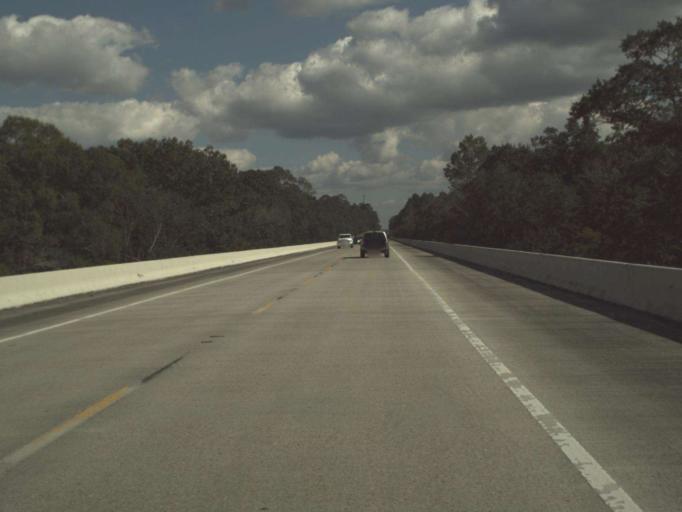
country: US
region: Florida
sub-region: Bay County
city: Laguna Beach
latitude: 30.4503
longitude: -85.8958
